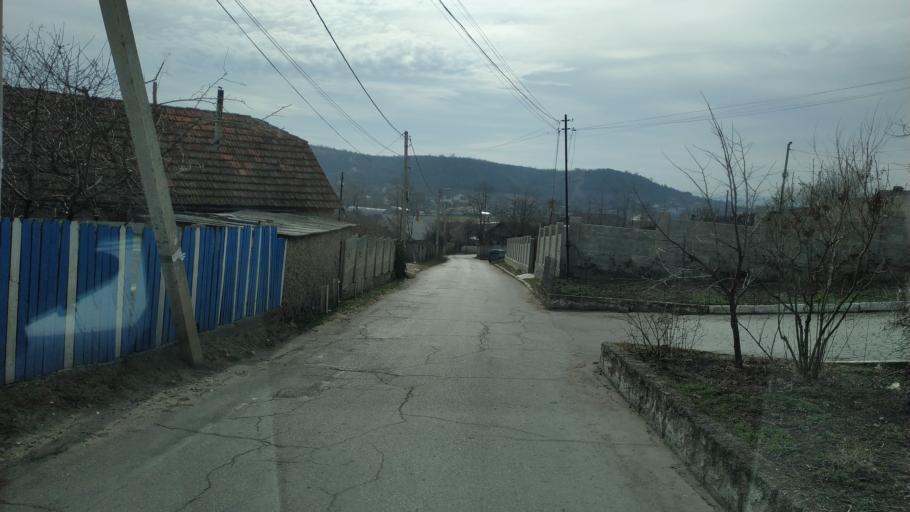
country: MD
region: Chisinau
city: Vatra
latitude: 47.0928
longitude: 28.7678
